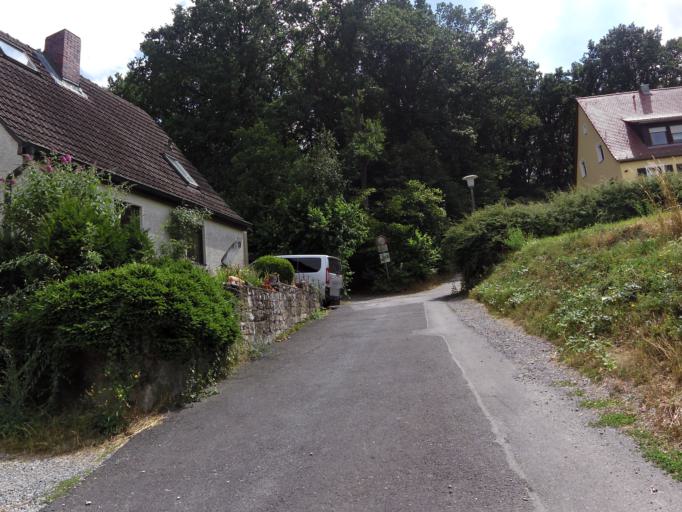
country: DE
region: Bavaria
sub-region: Regierungsbezirk Unterfranken
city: Gerbrunn
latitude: 49.7761
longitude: 9.9821
